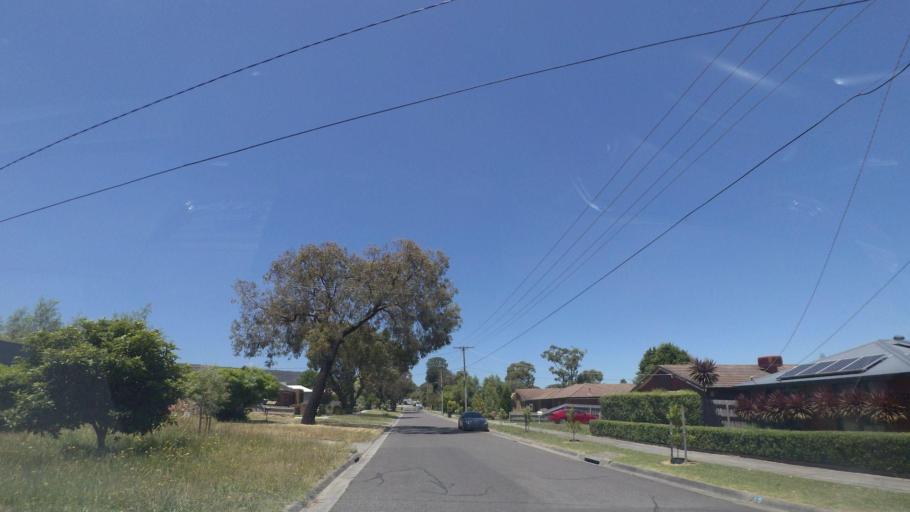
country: AU
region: Victoria
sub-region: Knox
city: Boronia
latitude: -37.8780
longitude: 145.2758
